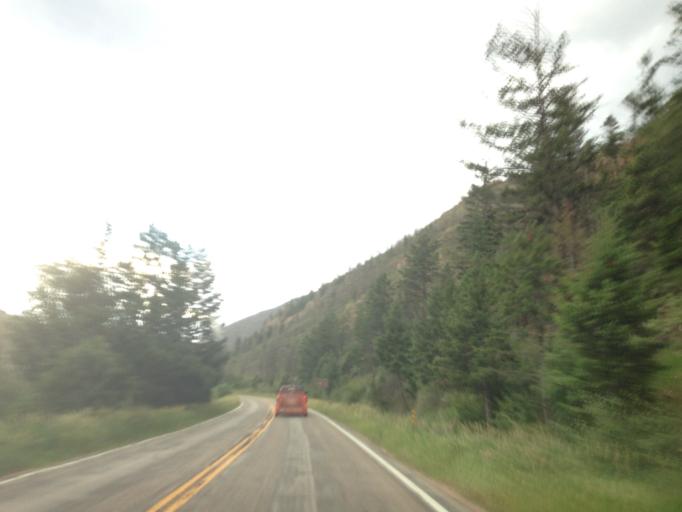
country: US
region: Colorado
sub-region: Larimer County
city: Laporte
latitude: 40.6822
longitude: -105.4056
